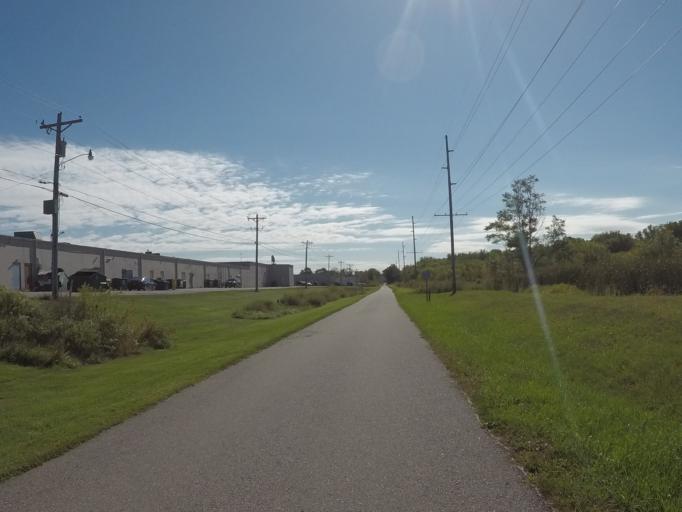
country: US
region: Wisconsin
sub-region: Richland County
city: Richland Center
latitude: 43.3177
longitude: -90.3639
